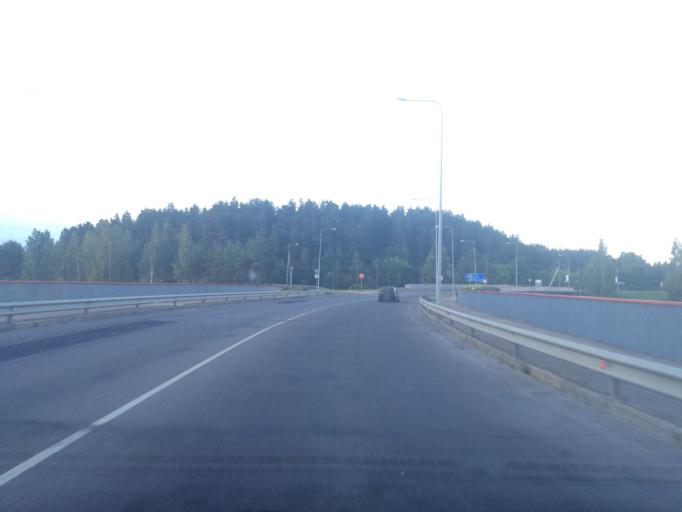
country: LT
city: Zarasai
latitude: 55.7253
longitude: 26.2465
